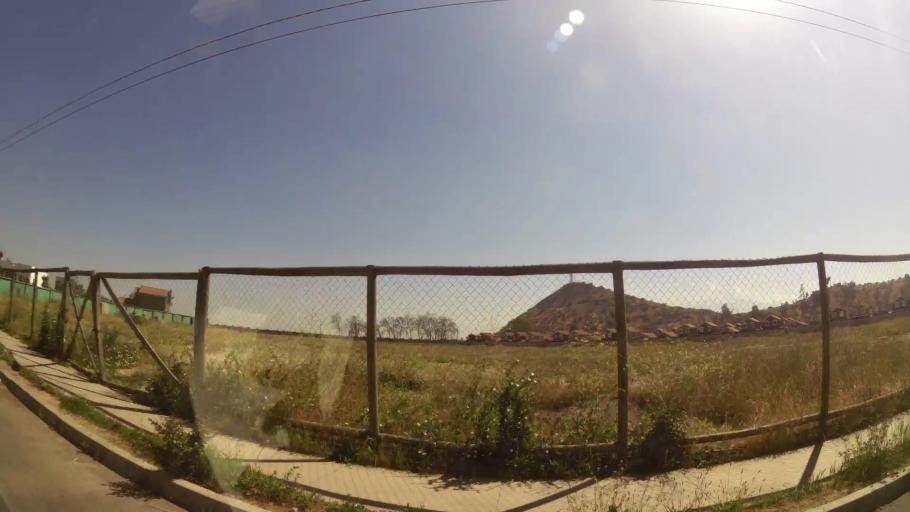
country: CL
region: Santiago Metropolitan
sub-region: Provincia de Maipo
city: San Bernardo
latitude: -33.6191
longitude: -70.6810
